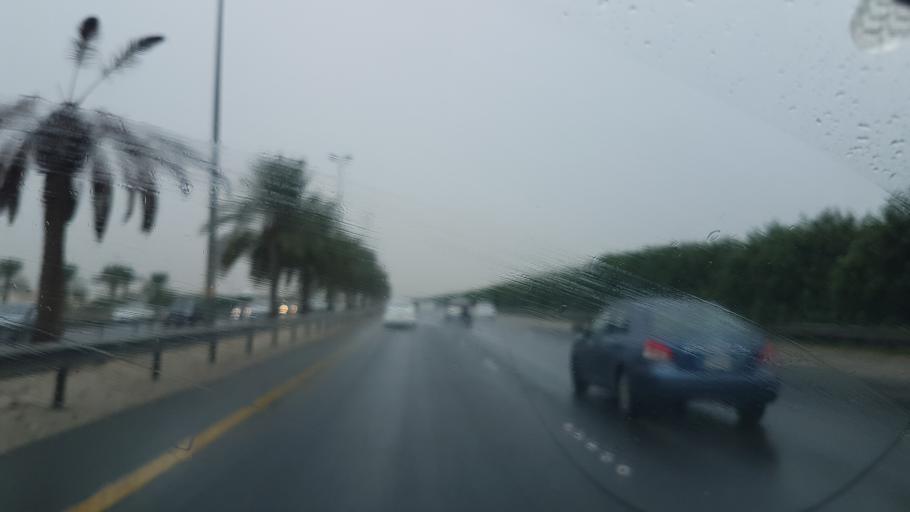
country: BH
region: Northern
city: Madinat `Isa
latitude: 26.1648
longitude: 50.5036
